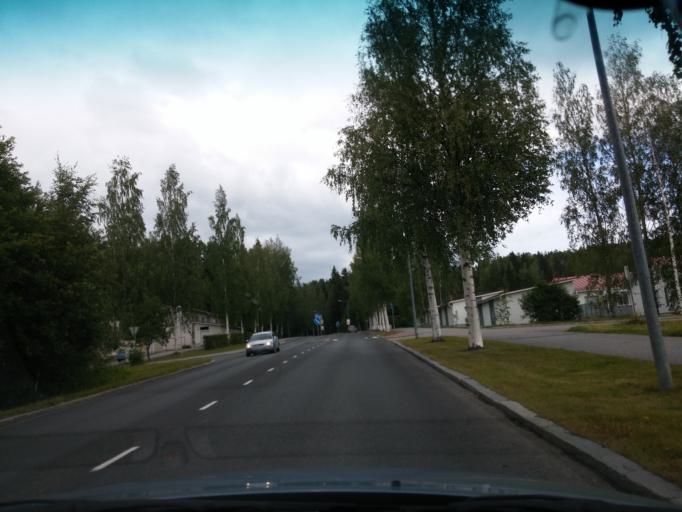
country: FI
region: Northern Savo
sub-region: Kuopio
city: Kuopio
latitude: 62.8410
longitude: 27.6572
